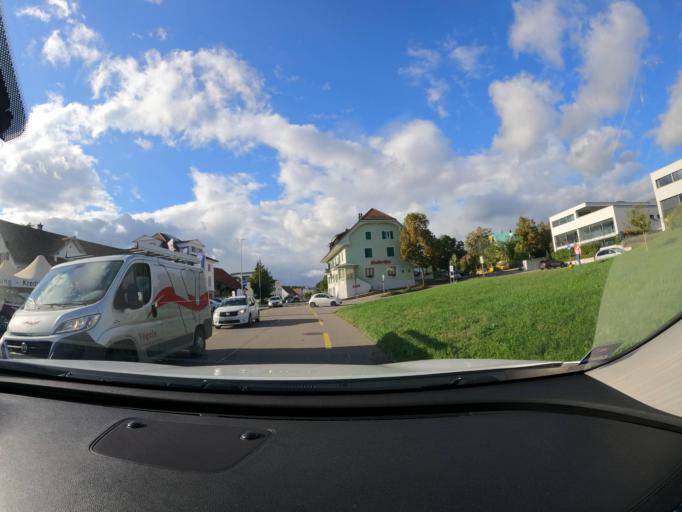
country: CH
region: Aargau
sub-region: Bezirk Brugg
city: Hausen
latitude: 47.4558
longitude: 8.2144
